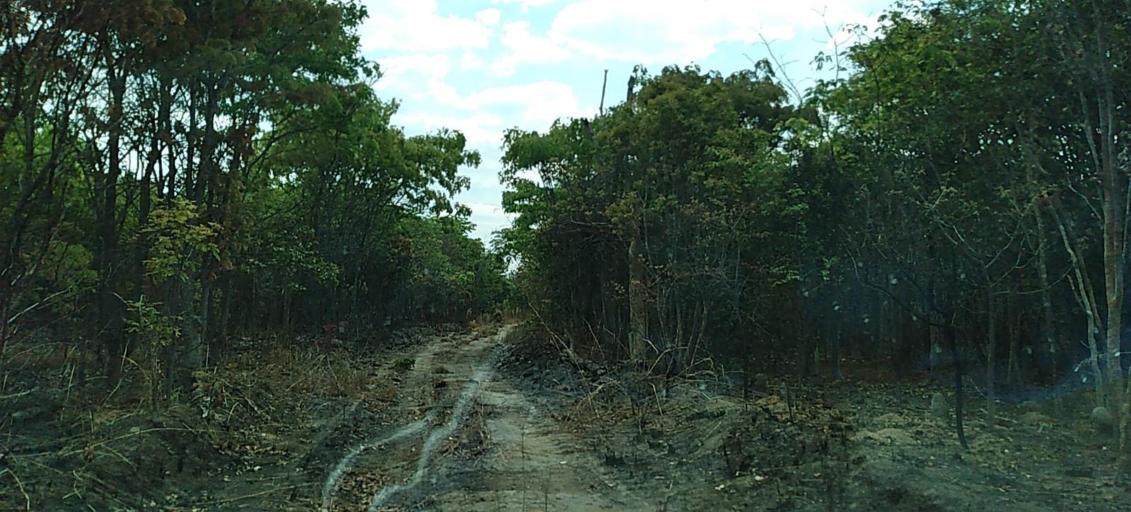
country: ZM
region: Copperbelt
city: Chililabombwe
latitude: -12.3303
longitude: 27.7677
